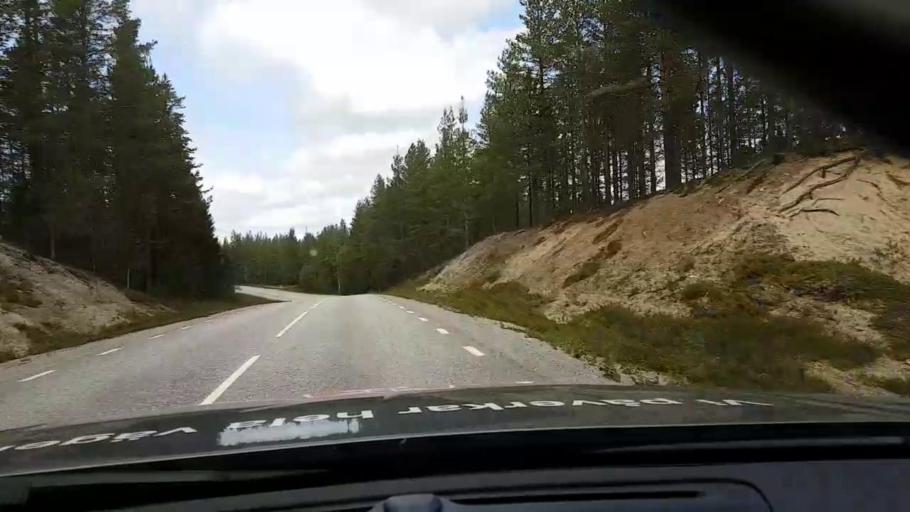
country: SE
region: Vaesternorrland
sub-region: OErnskoeldsviks Kommun
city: Bredbyn
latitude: 63.7018
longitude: 17.7635
